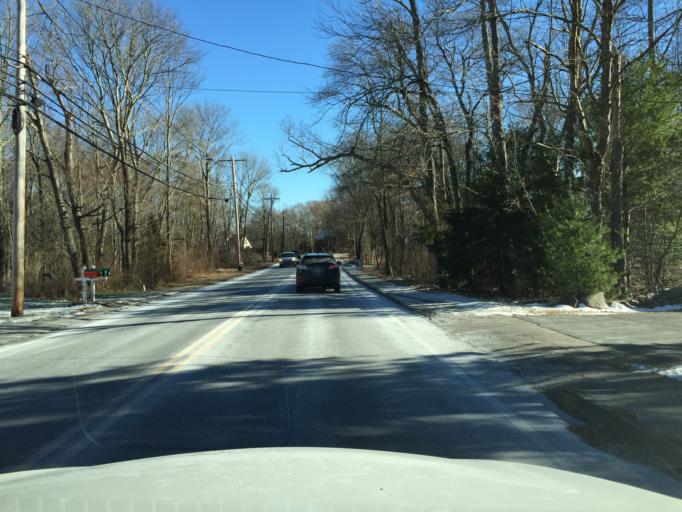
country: US
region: Massachusetts
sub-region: Norfolk County
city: Foxborough
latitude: 42.0632
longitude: -71.2239
